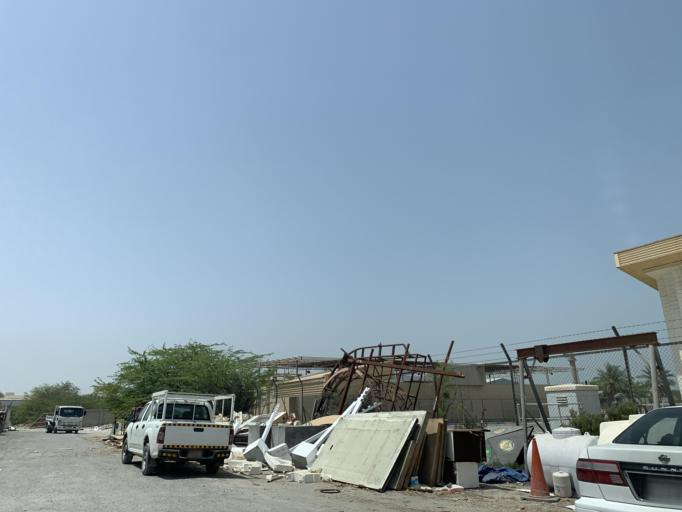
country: BH
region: Northern
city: Madinat `Isa
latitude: 26.1946
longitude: 50.5490
